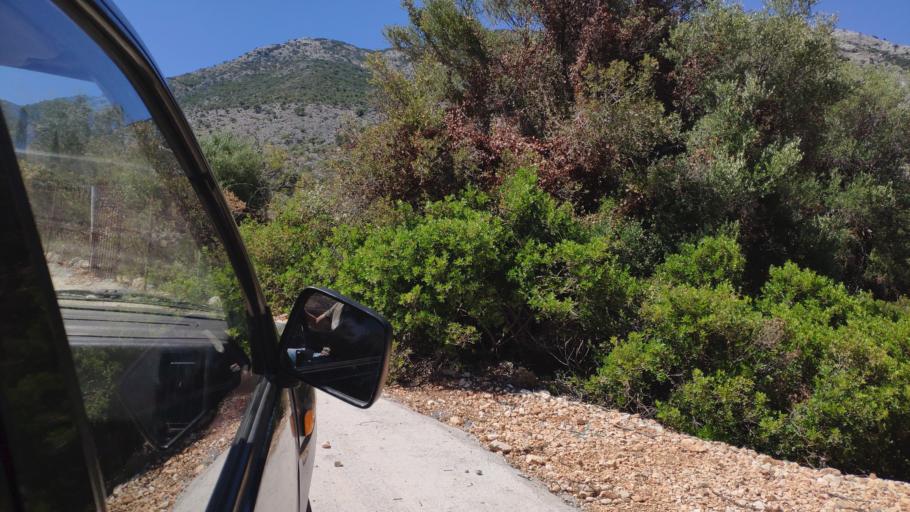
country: GR
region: West Greece
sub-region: Nomos Aitolias kai Akarnanias
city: Kandila
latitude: 38.6184
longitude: 20.9196
